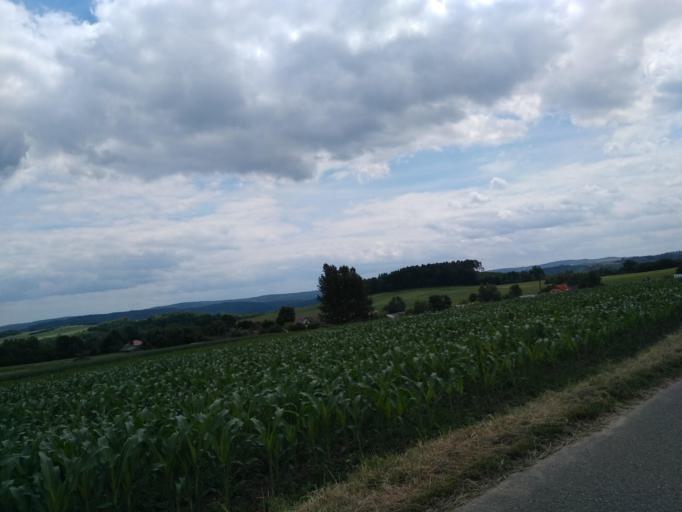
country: PL
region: Subcarpathian Voivodeship
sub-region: Powiat przeworski
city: Jawornik Polski
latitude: 49.8399
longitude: 22.2969
